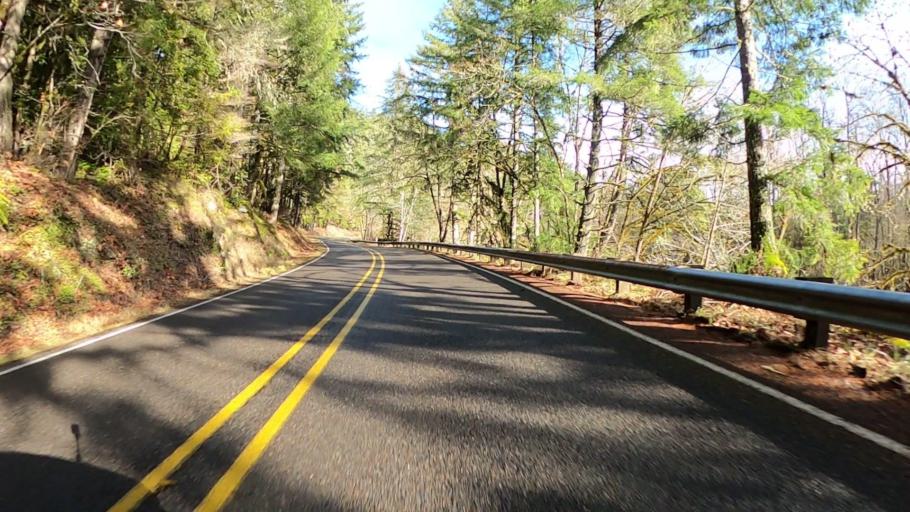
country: US
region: Oregon
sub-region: Lane County
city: Oakridge
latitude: 43.7481
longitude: -122.5143
